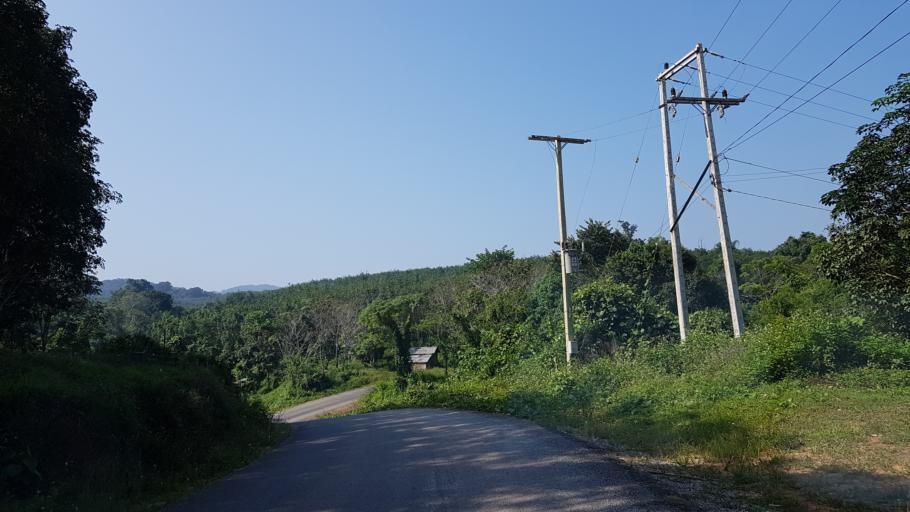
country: LA
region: Oudomxai
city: Muang Xay
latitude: 20.7094
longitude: 102.0811
